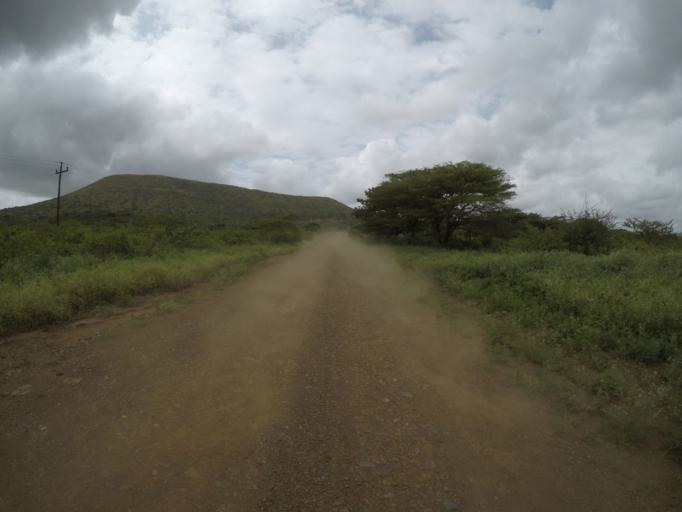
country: ZA
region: KwaZulu-Natal
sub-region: uThungulu District Municipality
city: Empangeni
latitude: -28.5972
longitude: 31.8921
